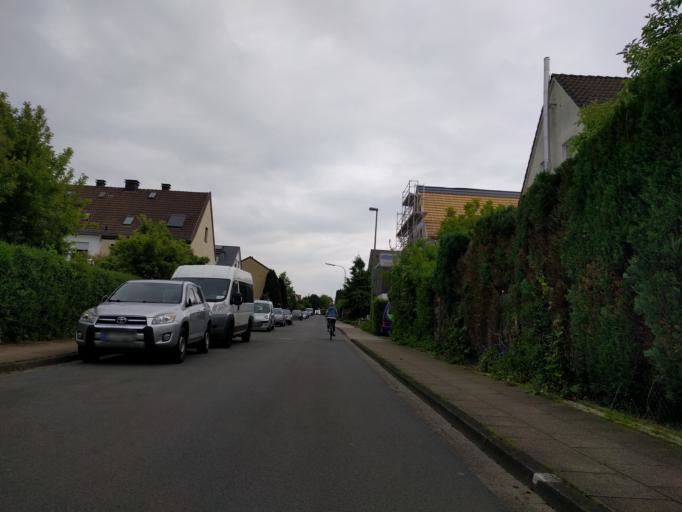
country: DE
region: North Rhine-Westphalia
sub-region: Regierungsbezirk Detmold
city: Bielefeld
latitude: 52.0495
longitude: 8.5406
